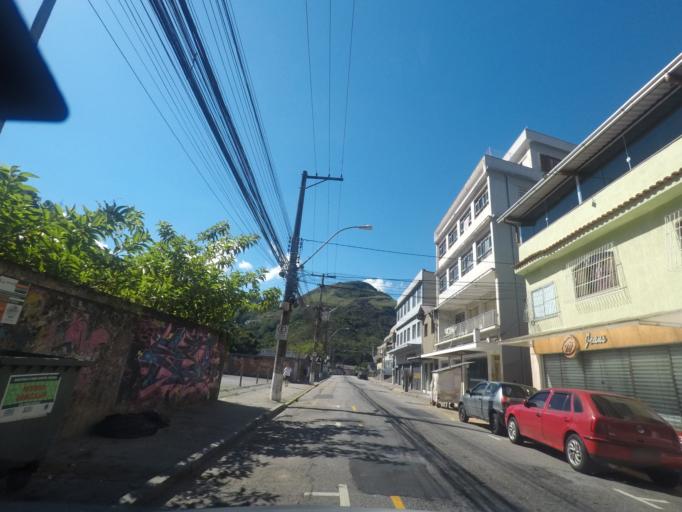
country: BR
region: Rio de Janeiro
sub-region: Petropolis
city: Petropolis
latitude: -22.5172
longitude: -43.1701
